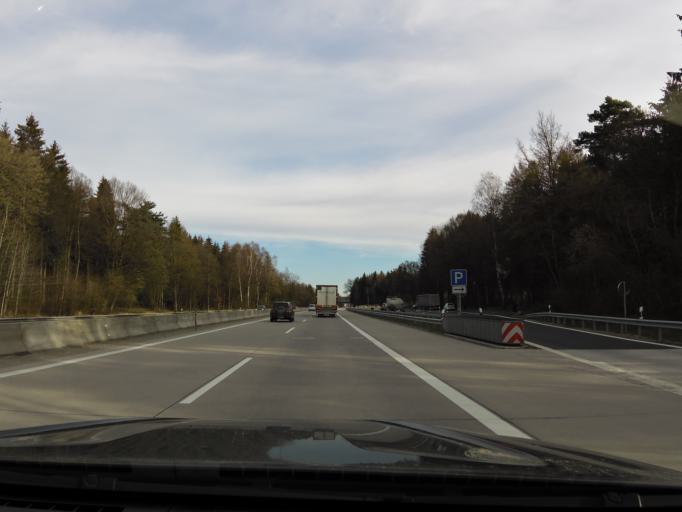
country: DE
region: Bavaria
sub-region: Upper Bavaria
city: Raubling
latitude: 47.7816
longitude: 12.0924
